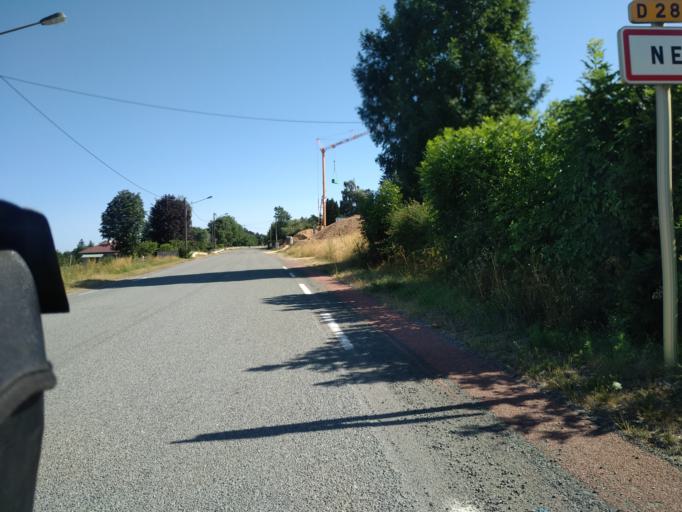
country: FR
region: Rhone-Alpes
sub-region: Departement de la Loire
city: Neulise
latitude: 45.8927
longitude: 4.1798
